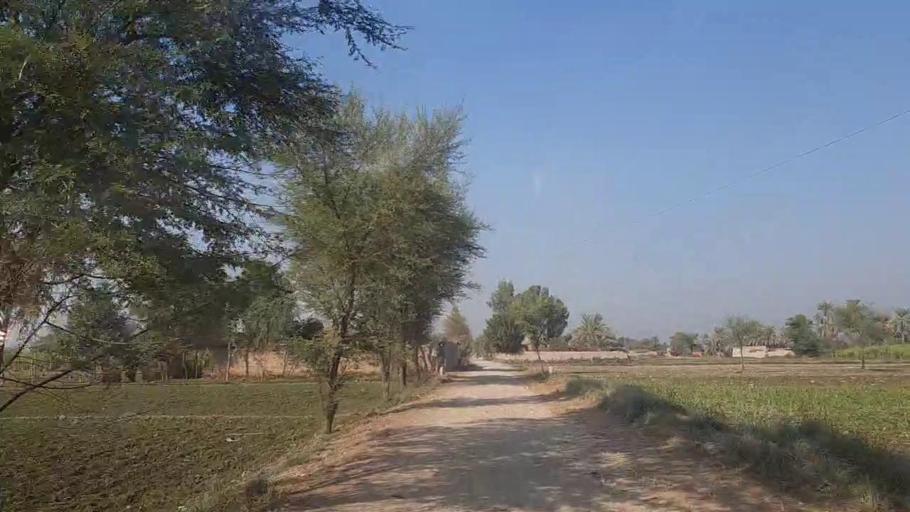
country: PK
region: Sindh
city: Gambat
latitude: 27.3687
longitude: 68.4748
